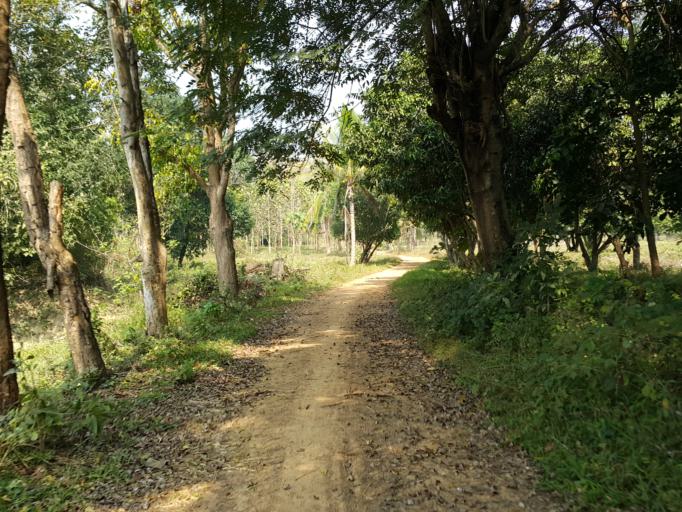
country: TH
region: Sukhothai
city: Thung Saliam
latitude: 17.3157
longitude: 99.5006
